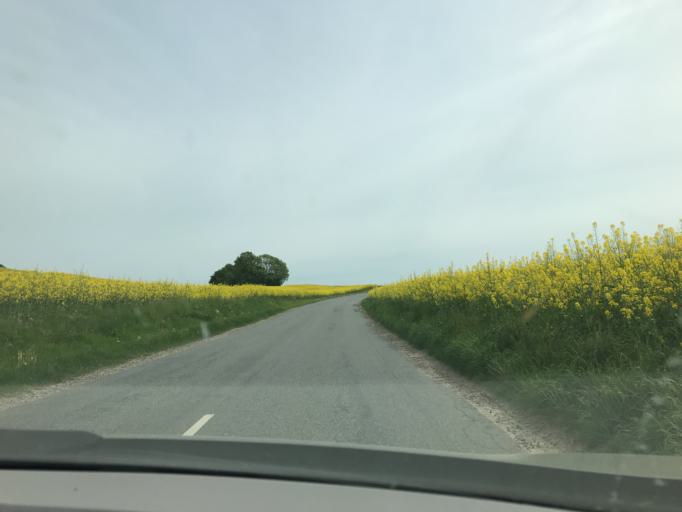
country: DK
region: Central Jutland
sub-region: Norddjurs Kommune
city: Allingabro
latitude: 56.5704
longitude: 10.2975
